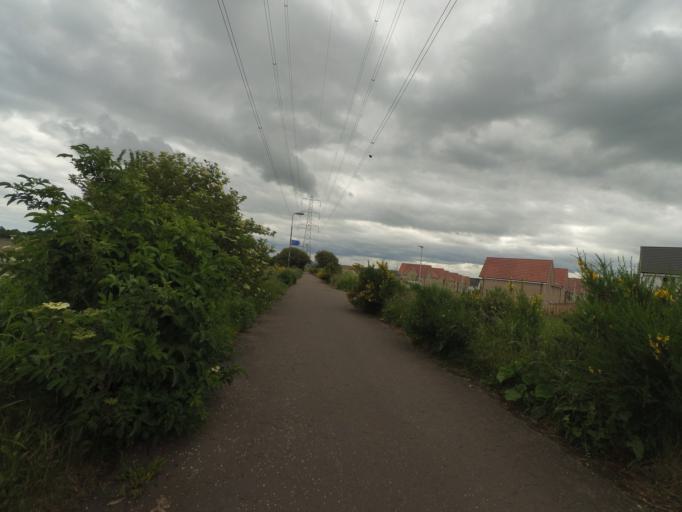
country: GB
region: Scotland
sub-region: East Lothian
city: Musselburgh
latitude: 55.9376
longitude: -3.0920
